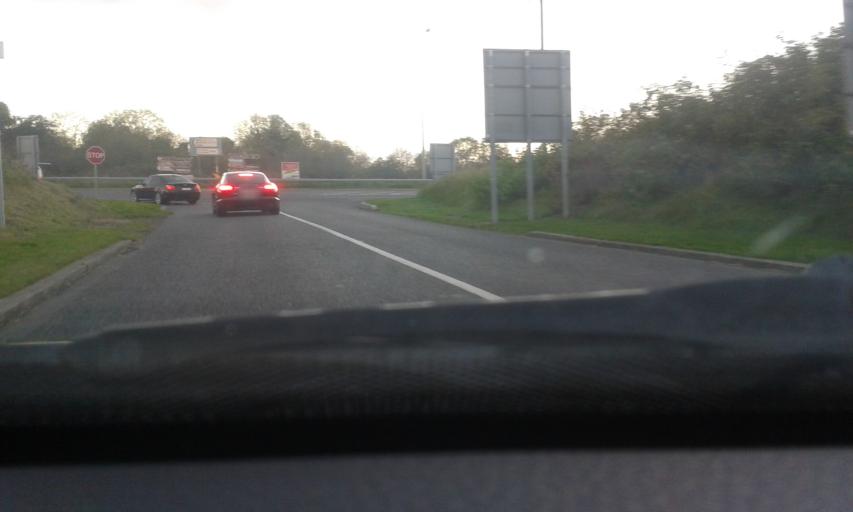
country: IE
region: Leinster
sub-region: Kildare
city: Cherryville
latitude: 53.1467
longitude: -7.0151
